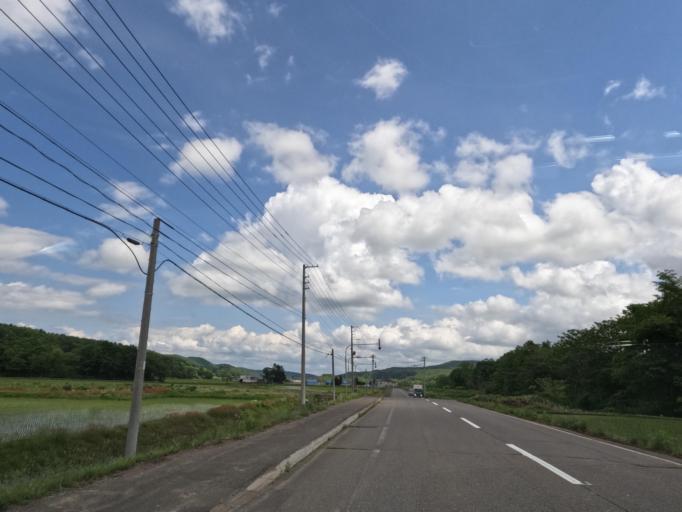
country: JP
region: Hokkaido
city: Takikawa
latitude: 43.5873
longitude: 141.7675
